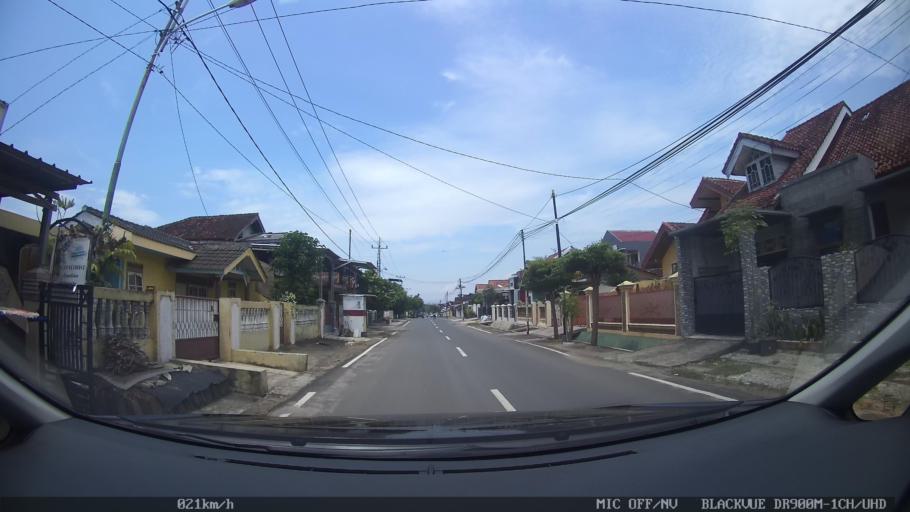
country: ID
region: Lampung
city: Kedaton
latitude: -5.3692
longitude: 105.3028
